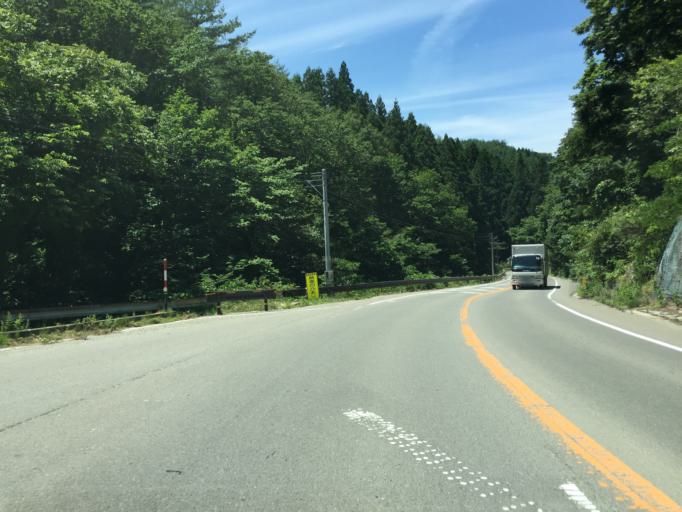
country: JP
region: Fukushima
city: Yanagawamachi-saiwaicho
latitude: 37.7544
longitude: 140.6861
